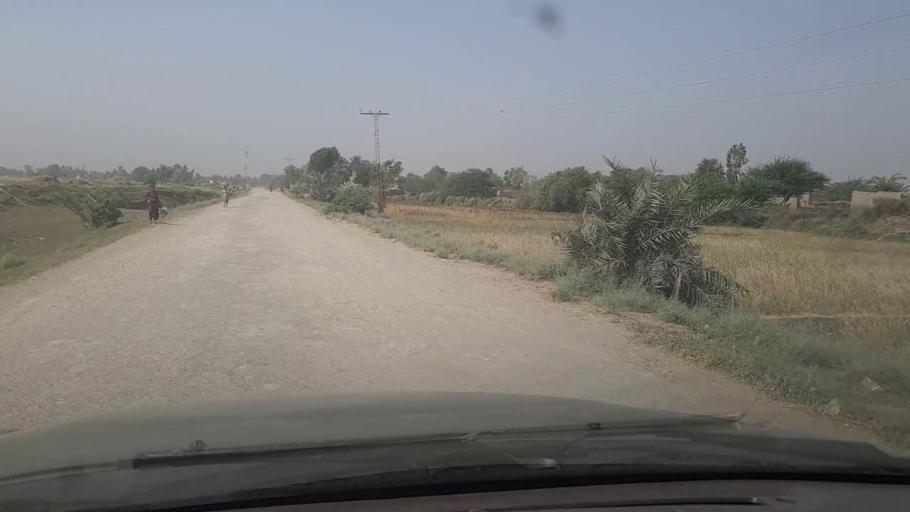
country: PK
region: Sindh
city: Garhi Yasin
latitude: 27.8679
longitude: 68.5554
